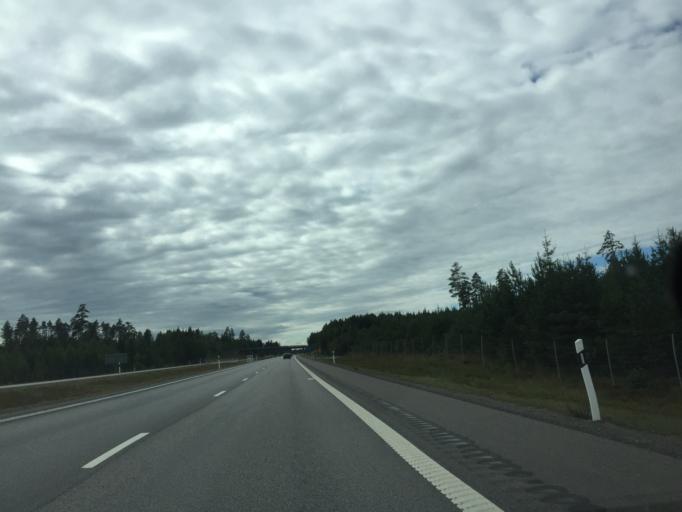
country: SE
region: OErebro
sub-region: Lindesbergs Kommun
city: Fellingsbro
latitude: 59.3486
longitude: 15.5542
